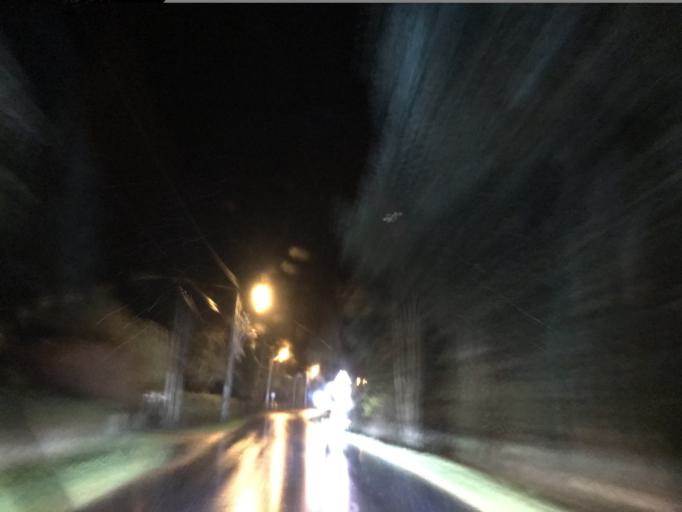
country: FR
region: Auvergne
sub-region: Departement du Puy-de-Dome
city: Celles-sur-Durolle
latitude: 45.8876
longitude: 3.6378
